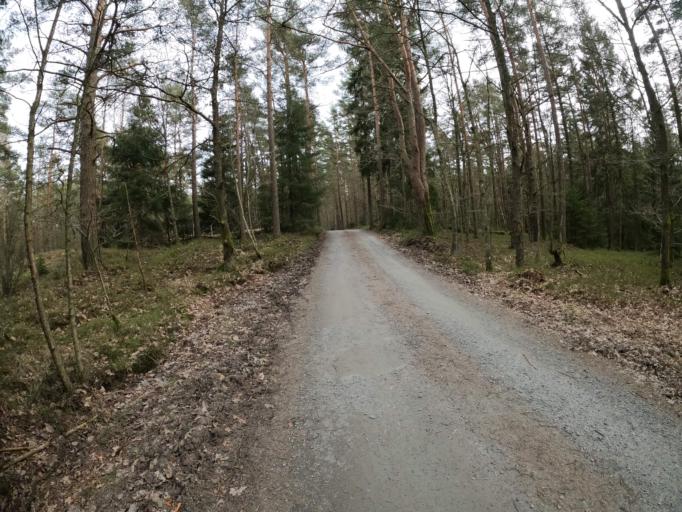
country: SE
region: Vaestra Goetaland
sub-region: Molndal
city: Kallered
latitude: 57.6231
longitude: 12.0758
